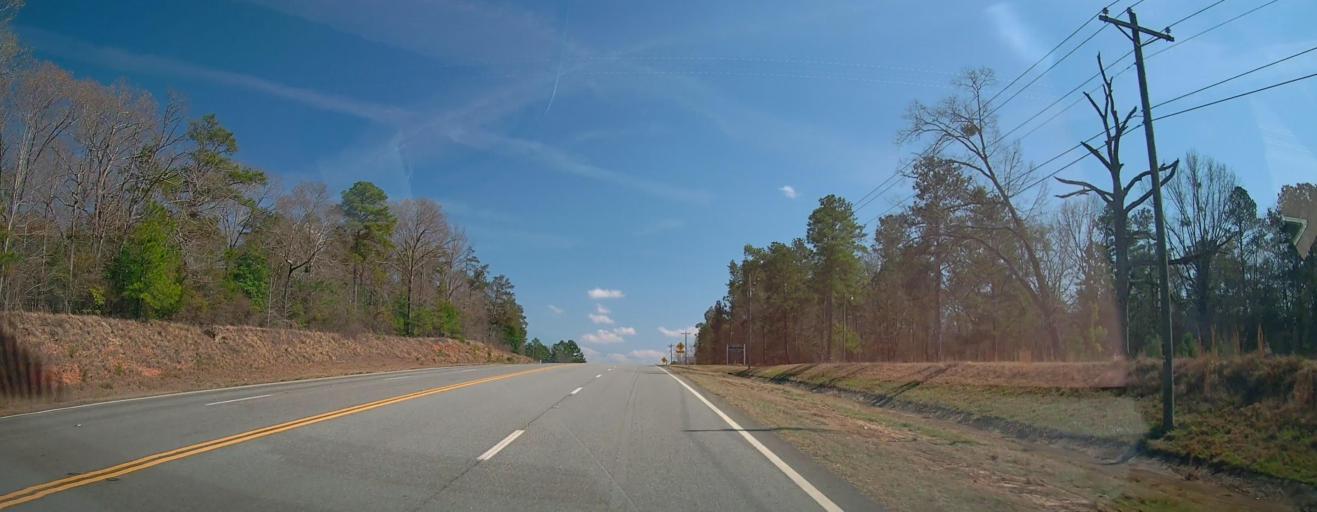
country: US
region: Georgia
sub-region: Wilkinson County
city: Gordon
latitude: 32.9110
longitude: -83.3825
